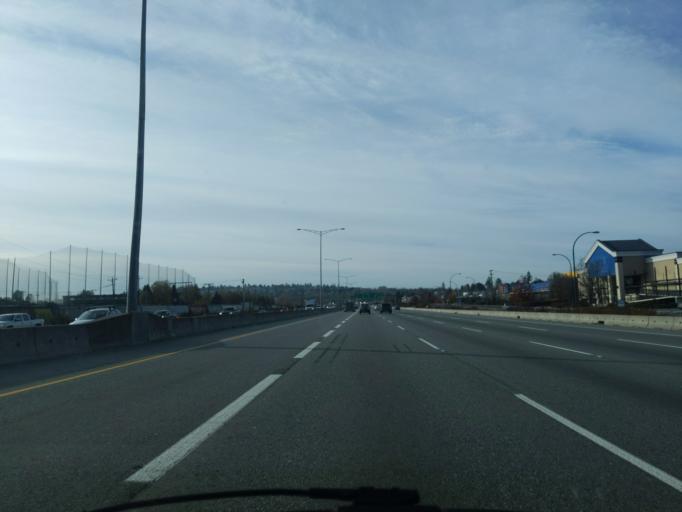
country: CA
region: British Columbia
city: Port Moody
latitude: 49.2330
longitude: -122.8612
